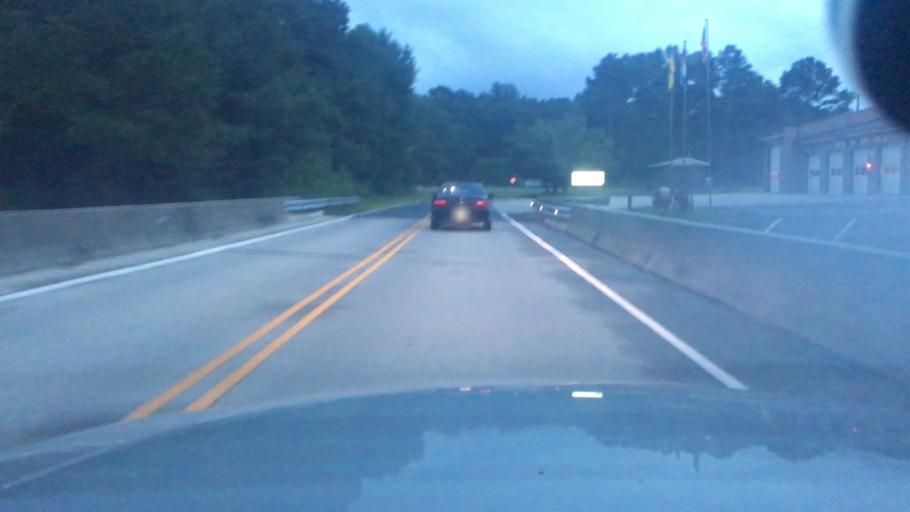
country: US
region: North Carolina
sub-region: Cumberland County
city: Hope Mills
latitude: 34.9618
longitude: -78.9245
